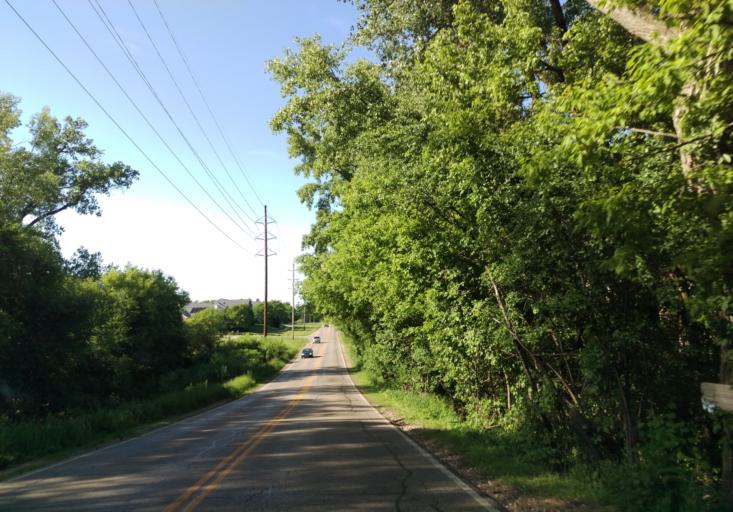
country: US
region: Wisconsin
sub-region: Dane County
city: Middleton
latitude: 43.0784
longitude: -89.5369
